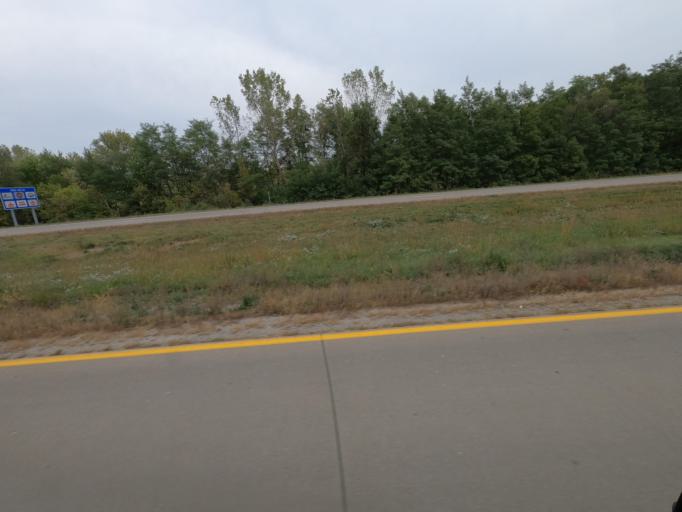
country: US
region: Iowa
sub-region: Marion County
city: Pella
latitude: 41.4015
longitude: -92.9377
